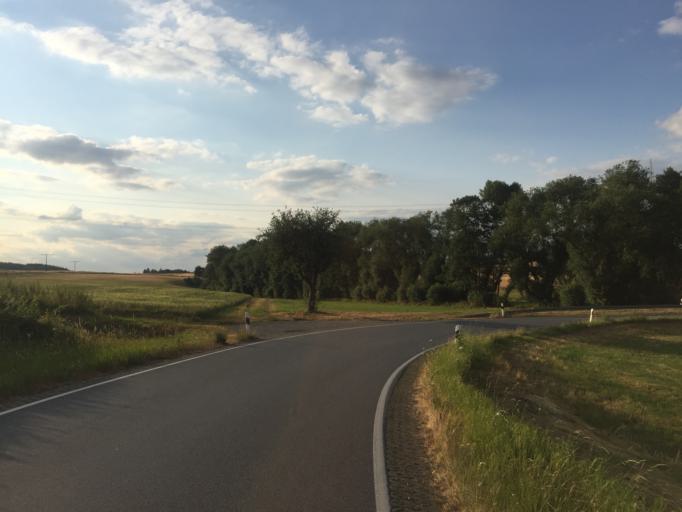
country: DE
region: Hesse
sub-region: Regierungsbezirk Giessen
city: Heuchelheim
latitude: 50.6015
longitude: 8.6163
